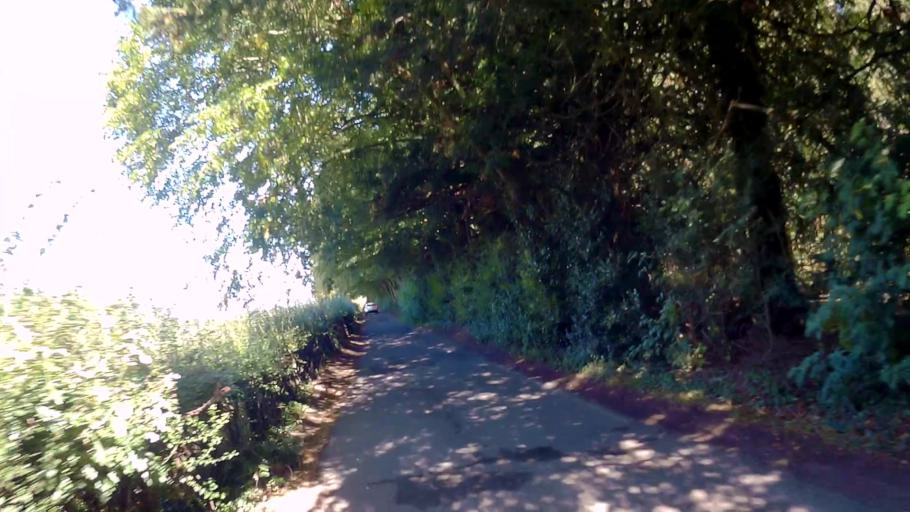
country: GB
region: England
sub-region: Hampshire
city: Andover
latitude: 51.1452
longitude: -1.4672
